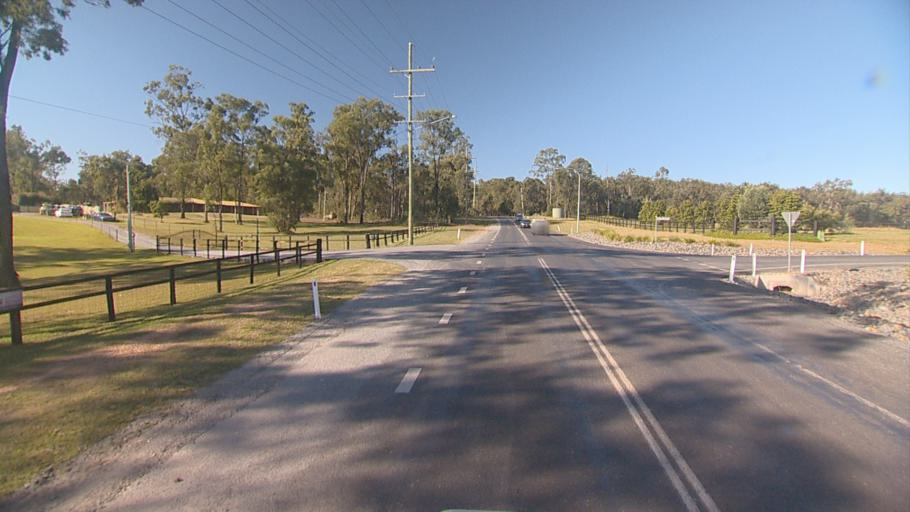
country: AU
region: Queensland
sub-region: Logan
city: Logan Reserve
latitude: -27.7459
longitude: 153.1393
